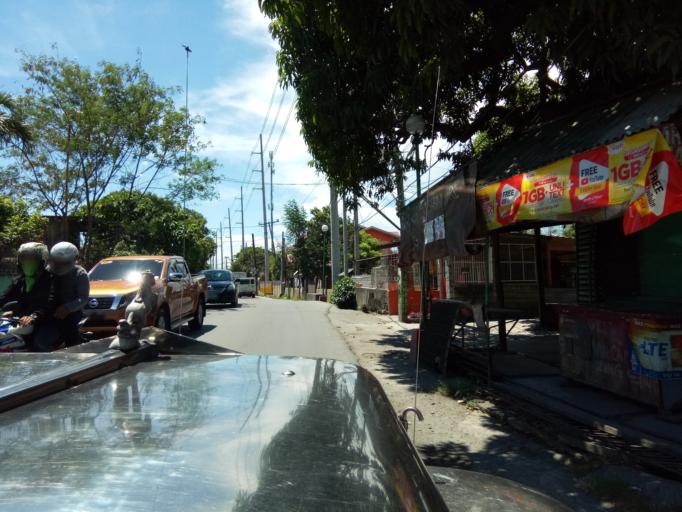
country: PH
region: Calabarzon
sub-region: Province of Cavite
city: General Trias
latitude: 14.3659
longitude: 120.8934
